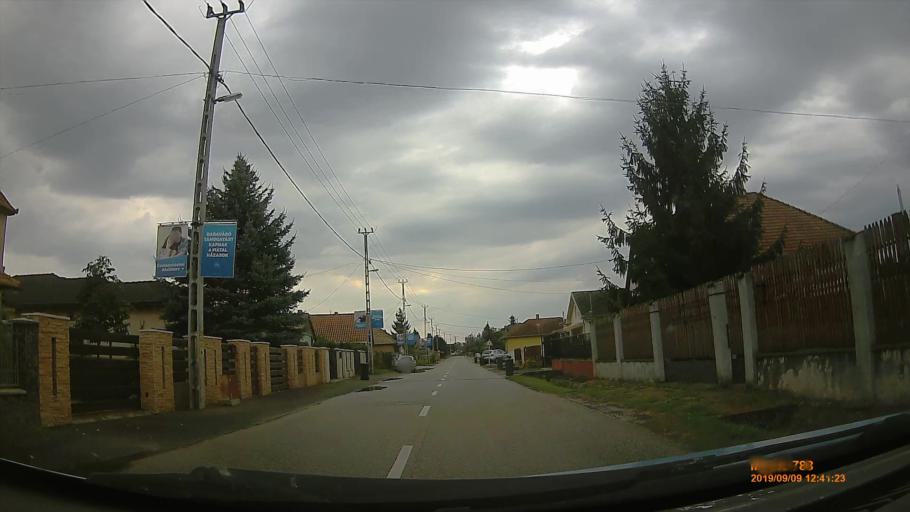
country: HU
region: Szabolcs-Szatmar-Bereg
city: Nyirpazony
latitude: 47.9802
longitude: 21.8015
